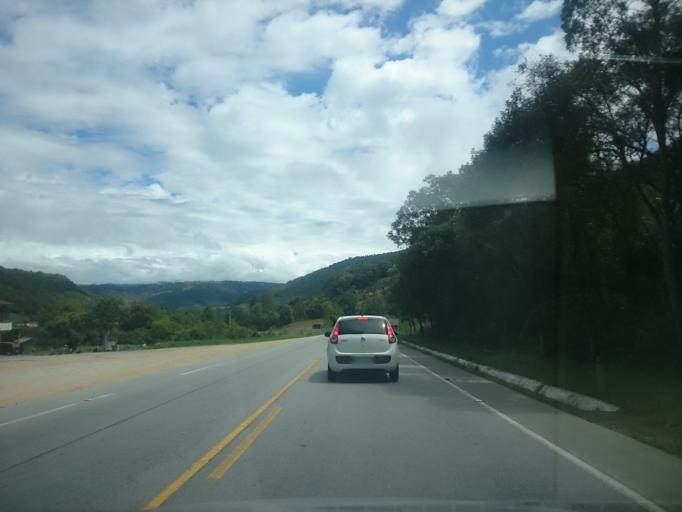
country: BR
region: Santa Catarina
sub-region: Anitapolis
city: Anitapolis
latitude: -27.6855
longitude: -49.2238
